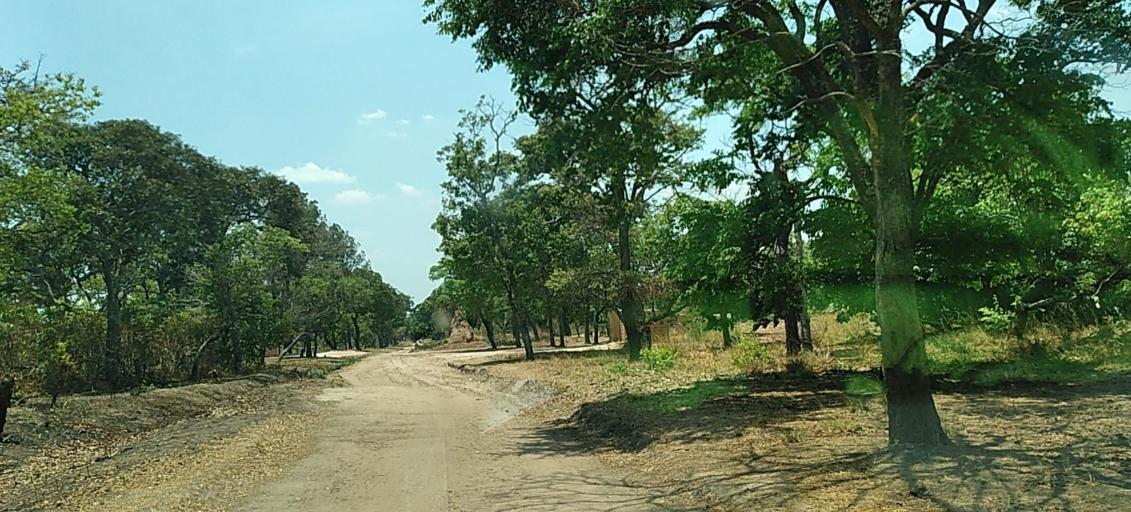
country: CD
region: Katanga
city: Kolwezi
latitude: -11.3779
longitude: 25.2168
